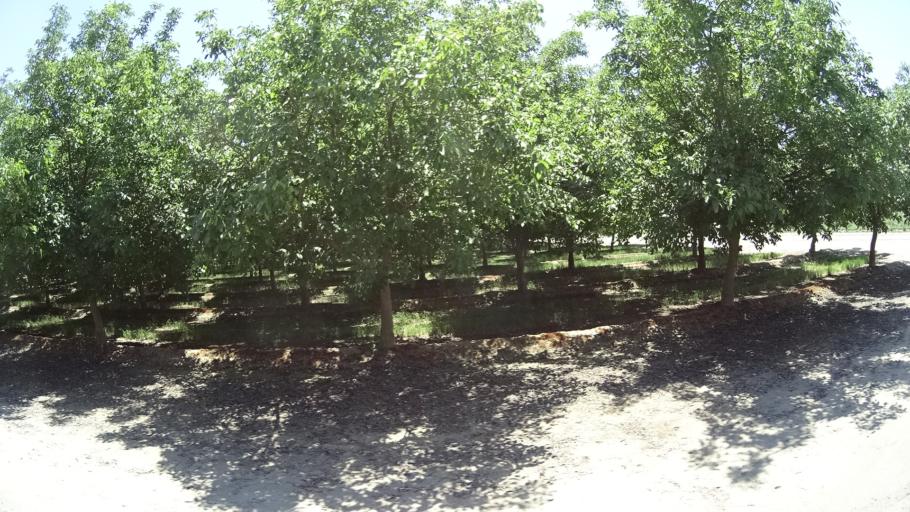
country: US
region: California
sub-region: Kings County
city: Lucerne
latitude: 36.4230
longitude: -119.6184
